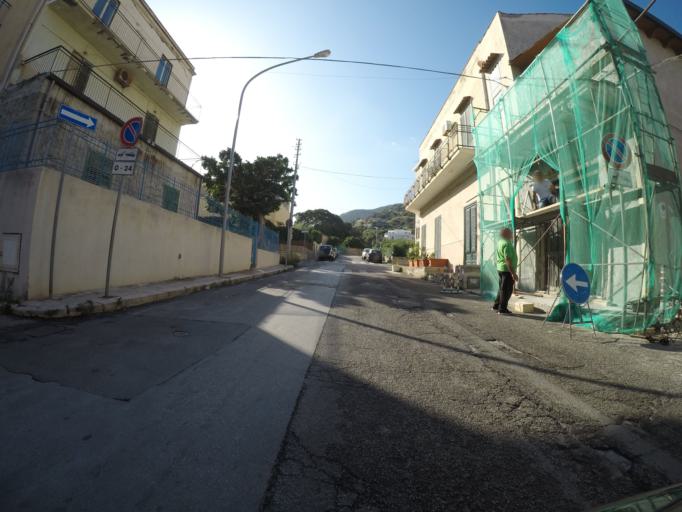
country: IT
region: Sicily
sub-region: Palermo
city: Isola delle Femmine
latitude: 38.1975
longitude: 13.2748
